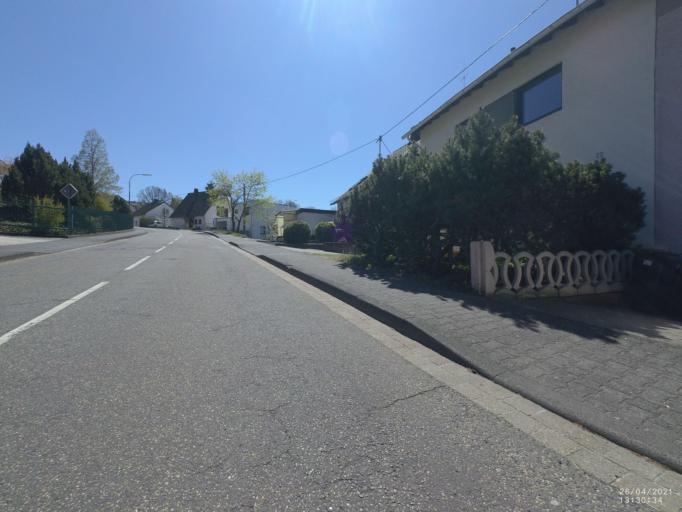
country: DE
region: Rheinland-Pfalz
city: Niederwerth
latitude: 50.3987
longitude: 7.6186
